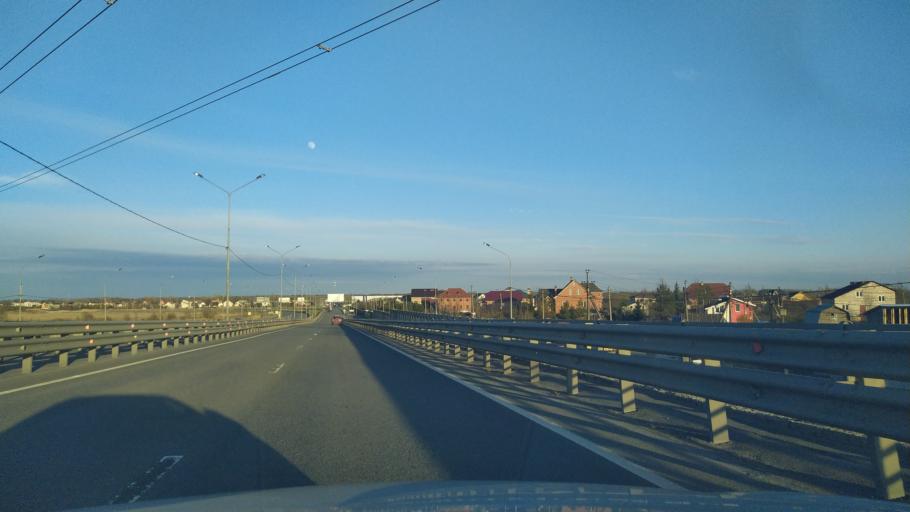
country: RU
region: St.-Petersburg
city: Aleksandrovskaya
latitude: 59.7434
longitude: 30.3131
